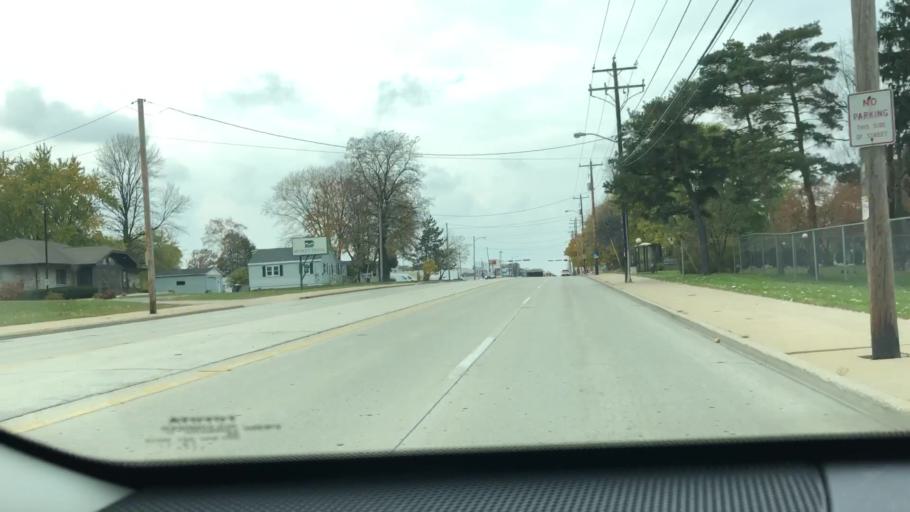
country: US
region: Wisconsin
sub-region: Brown County
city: Green Bay
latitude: 44.5212
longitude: -88.0567
